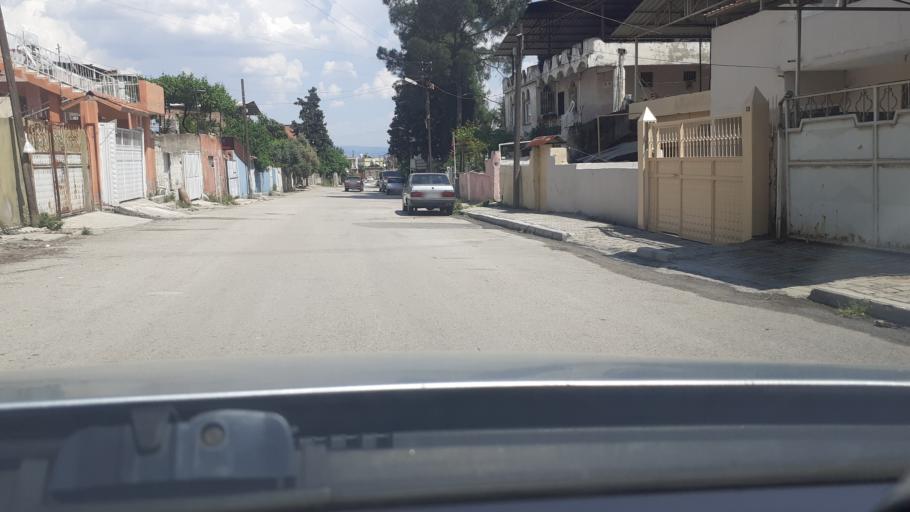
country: TR
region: Hatay
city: Kirikhan
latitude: 36.5022
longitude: 36.3567
